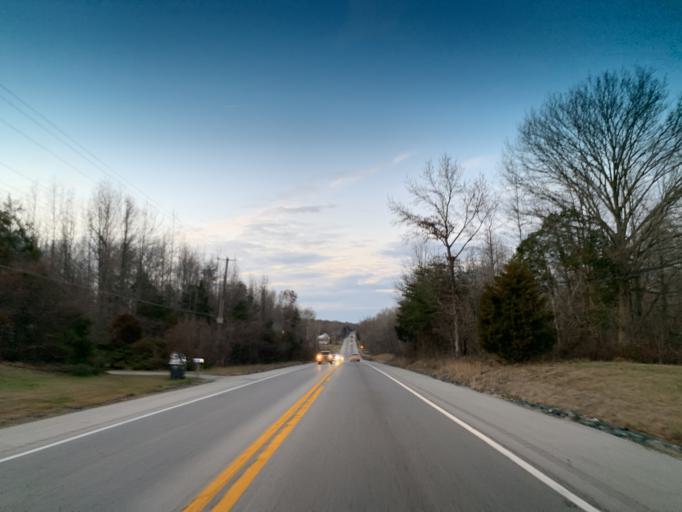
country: US
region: Maryland
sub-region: Cecil County
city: Elkton
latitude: 39.5685
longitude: -75.8123
